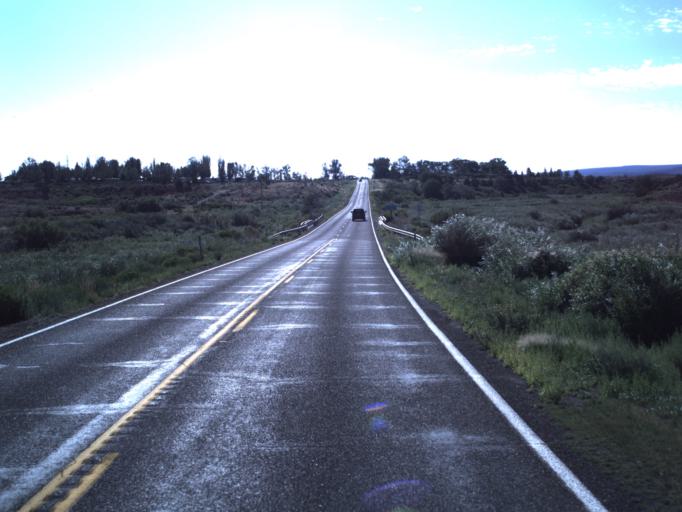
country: US
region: Utah
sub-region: Wayne County
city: Loa
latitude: 38.3022
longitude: -111.4516
